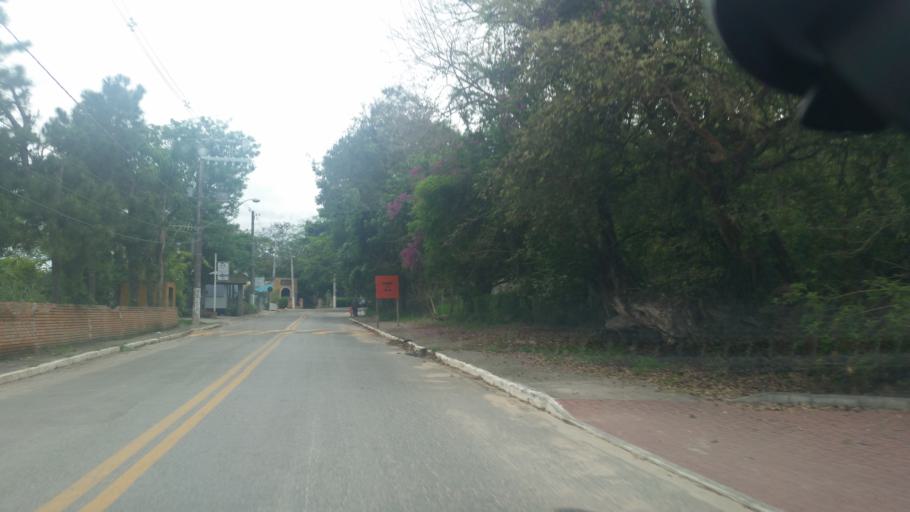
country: BR
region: Sao Paulo
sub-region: Taubate
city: Taubate
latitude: -23.0253
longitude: -45.6321
